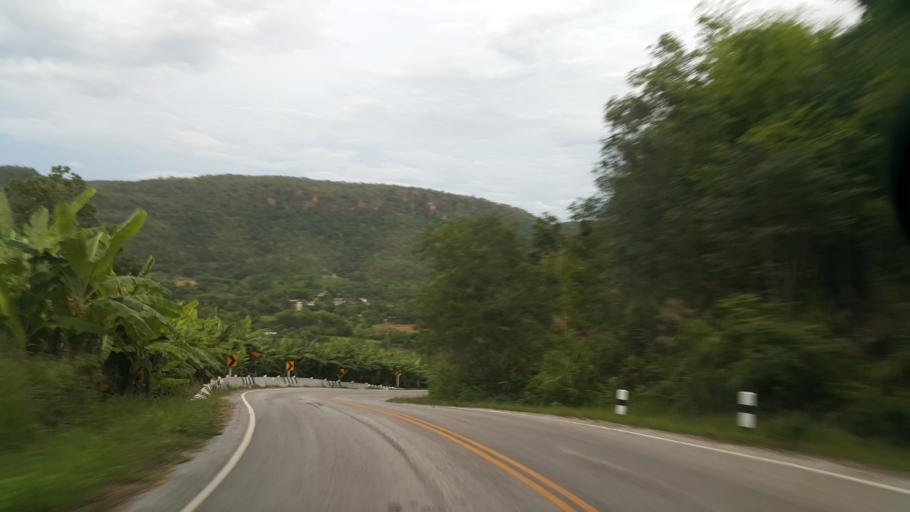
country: TH
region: Loei
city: Na Haeo
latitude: 17.4928
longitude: 101.1744
